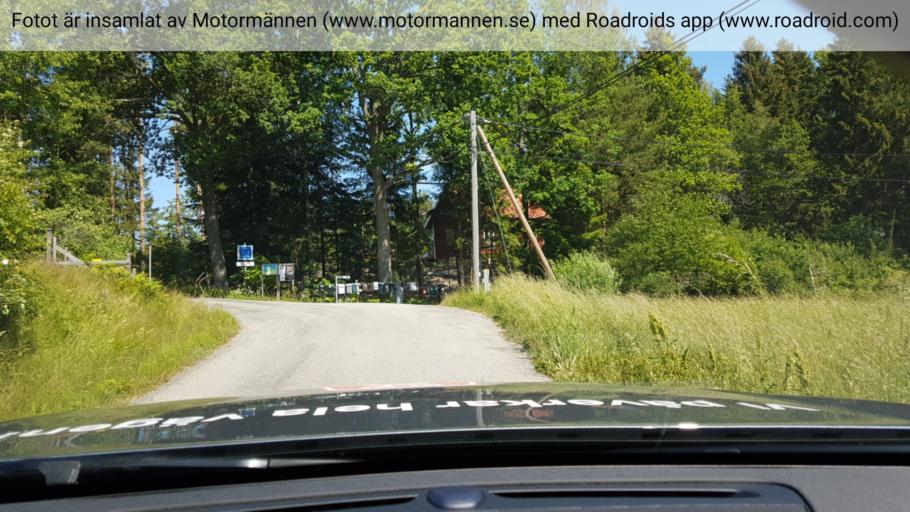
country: SE
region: Stockholm
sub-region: Haninge Kommun
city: Jordbro
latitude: 59.0167
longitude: 18.1154
